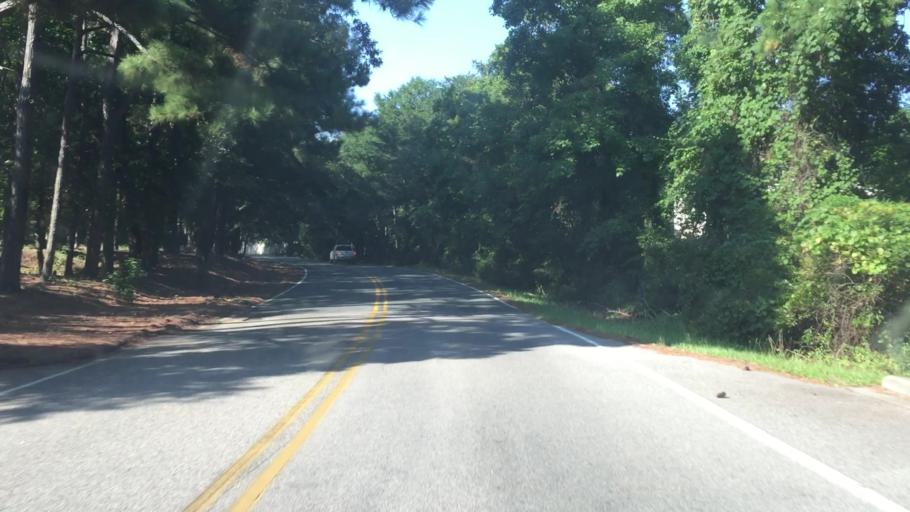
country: US
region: South Carolina
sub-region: Horry County
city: Myrtle Beach
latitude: 33.7531
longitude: -78.8061
